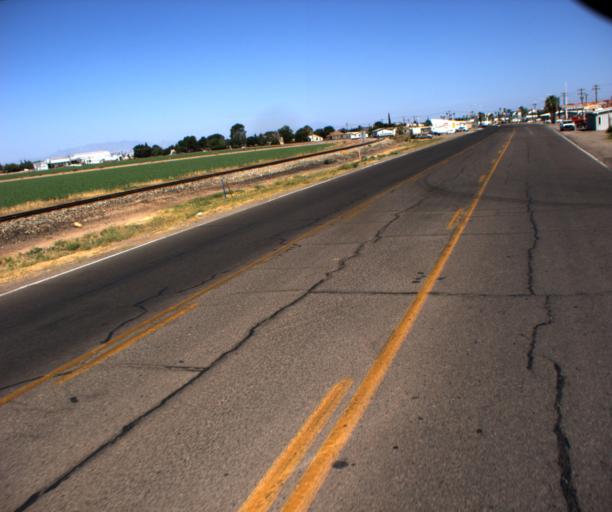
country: US
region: Arizona
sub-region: Graham County
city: Safford
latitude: 32.8297
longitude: -109.6965
